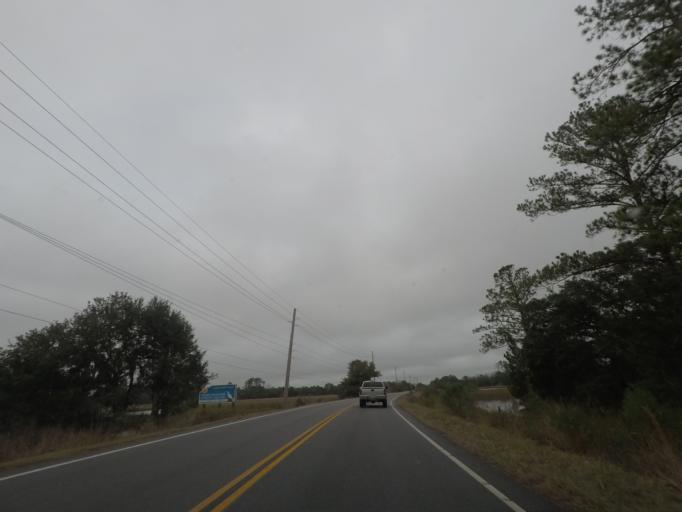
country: US
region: South Carolina
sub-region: Charleston County
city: Meggett
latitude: 32.6251
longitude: -80.3445
